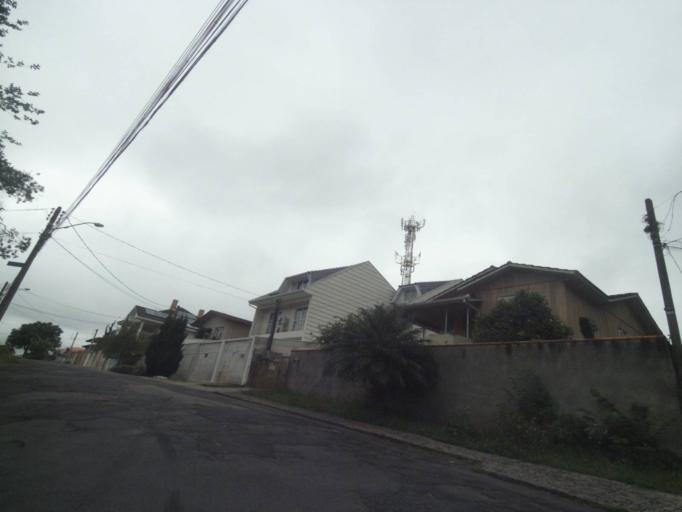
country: BR
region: Parana
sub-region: Curitiba
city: Curitiba
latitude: -25.3942
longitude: -49.2752
